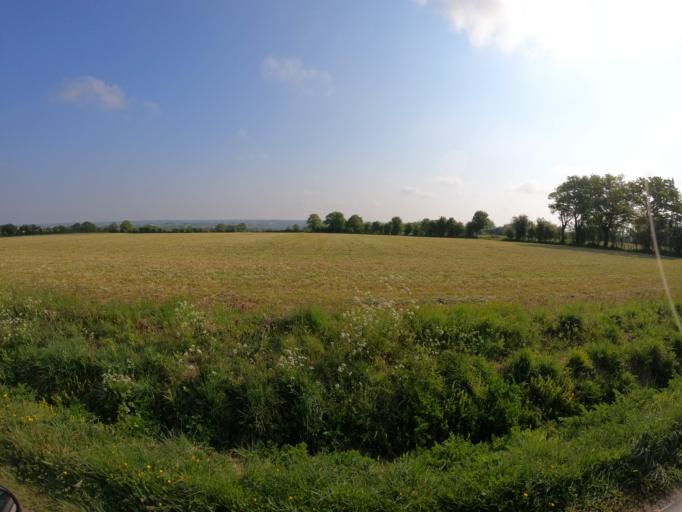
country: FR
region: Pays de la Loire
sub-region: Departement de Maine-et-Loire
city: La Romagne
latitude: 47.0651
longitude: -1.0431
